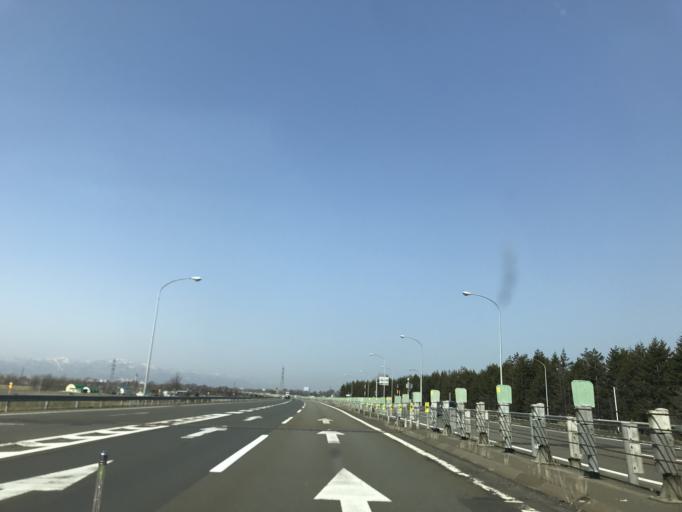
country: JP
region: Hokkaido
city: Ebetsu
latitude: 43.0937
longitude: 141.4965
